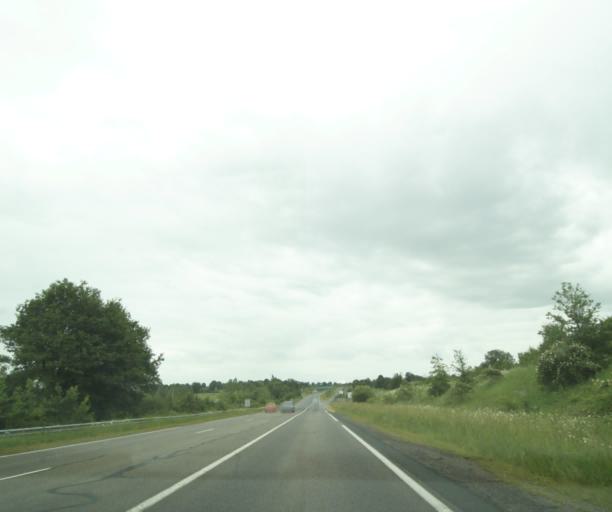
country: FR
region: Poitou-Charentes
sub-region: Departement des Deux-Sevres
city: Parthenay
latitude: 46.6476
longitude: -0.2728
